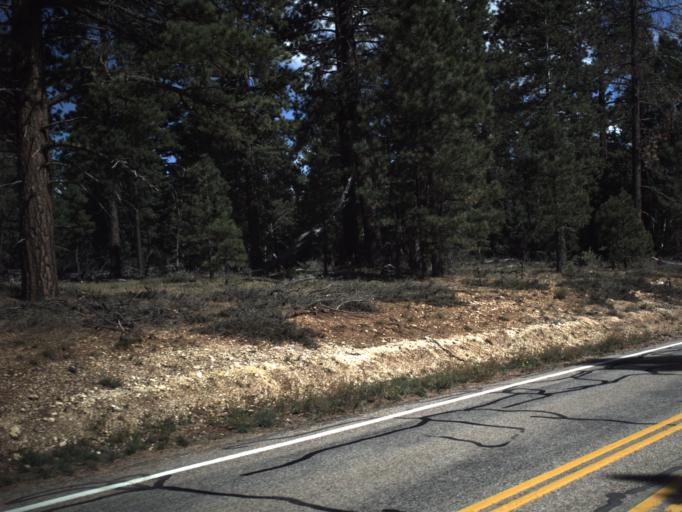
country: US
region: Utah
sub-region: Garfield County
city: Panguitch
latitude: 37.5165
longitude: -112.6442
